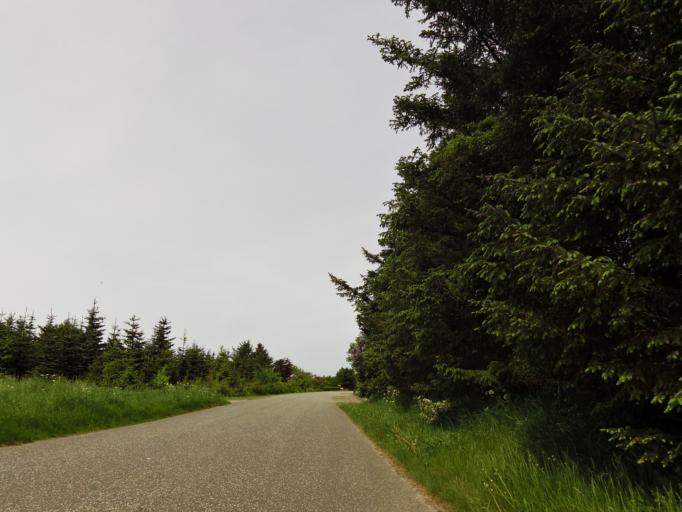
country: DK
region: Central Jutland
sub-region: Holstebro Kommune
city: Vinderup
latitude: 56.5616
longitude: 8.8896
